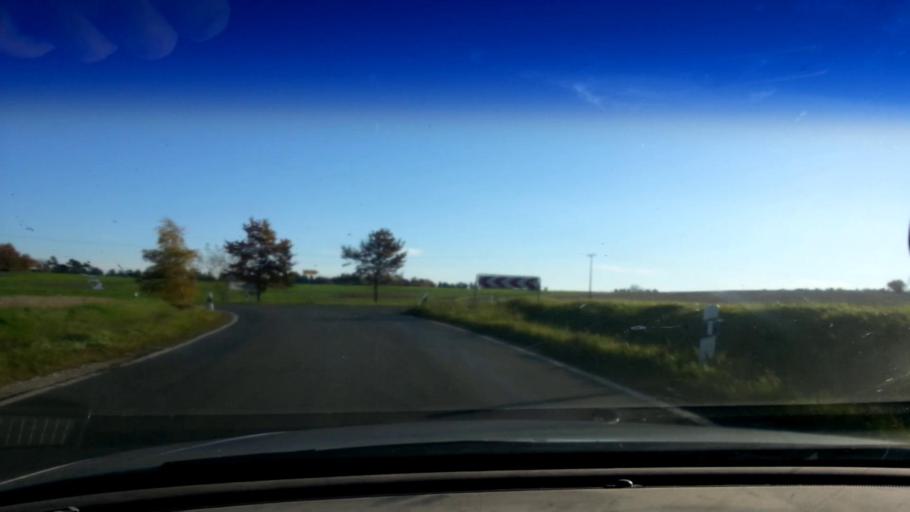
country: DE
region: Bavaria
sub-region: Upper Franconia
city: Poxdorf
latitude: 49.8962
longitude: 11.0932
